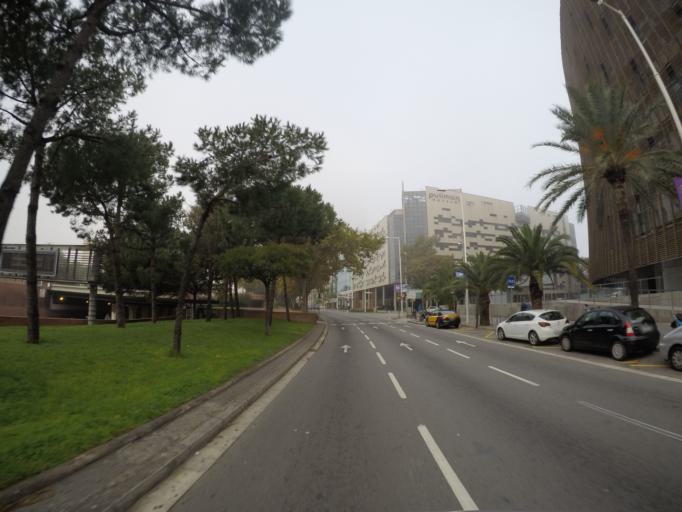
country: ES
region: Catalonia
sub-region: Provincia de Barcelona
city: Ciutat Vella
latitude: 41.3856
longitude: 2.1939
